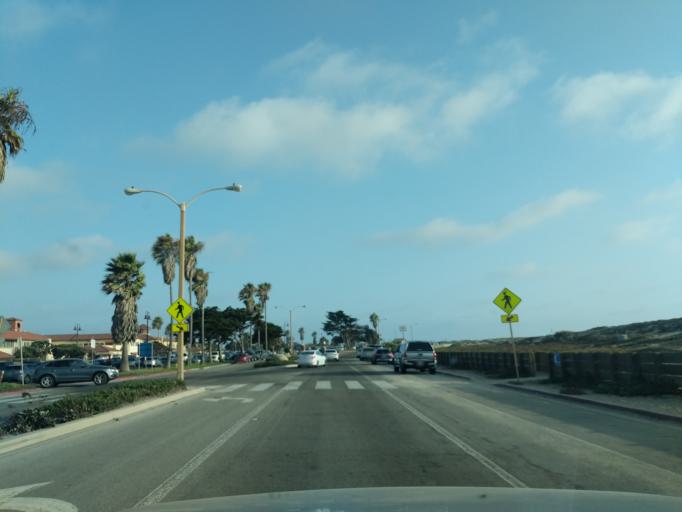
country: US
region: California
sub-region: Ventura County
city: Ventura
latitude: 34.2430
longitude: -119.2660
